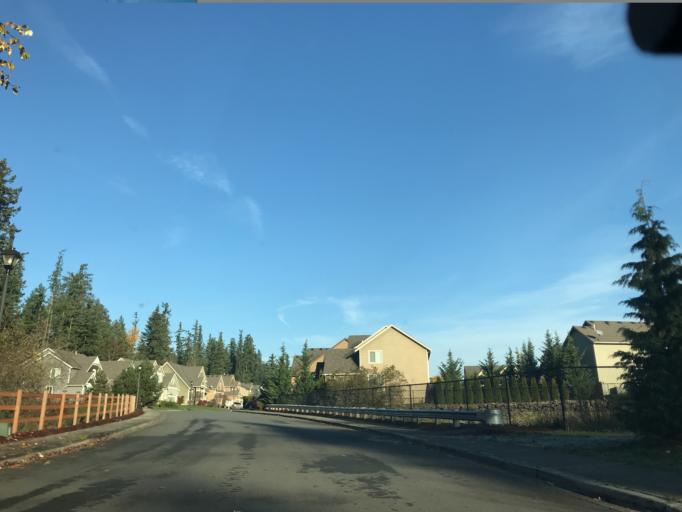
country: US
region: Washington
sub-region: King County
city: Black Diamond
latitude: 47.3122
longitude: -122.0243
